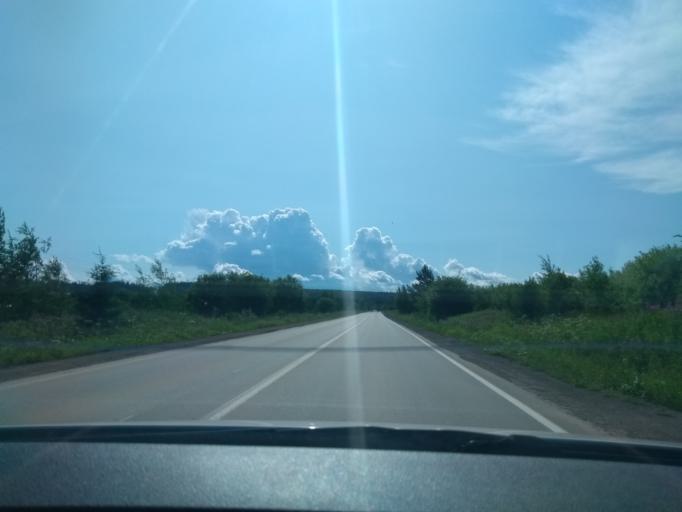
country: RU
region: Perm
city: Lobanovo
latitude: 57.8448
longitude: 56.3603
